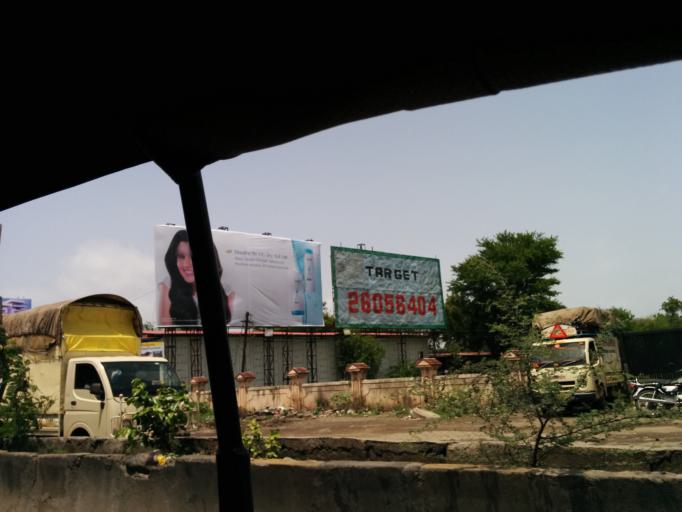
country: IN
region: Maharashtra
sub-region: Pune Division
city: Lohogaon
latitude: 18.5315
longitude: 73.9322
